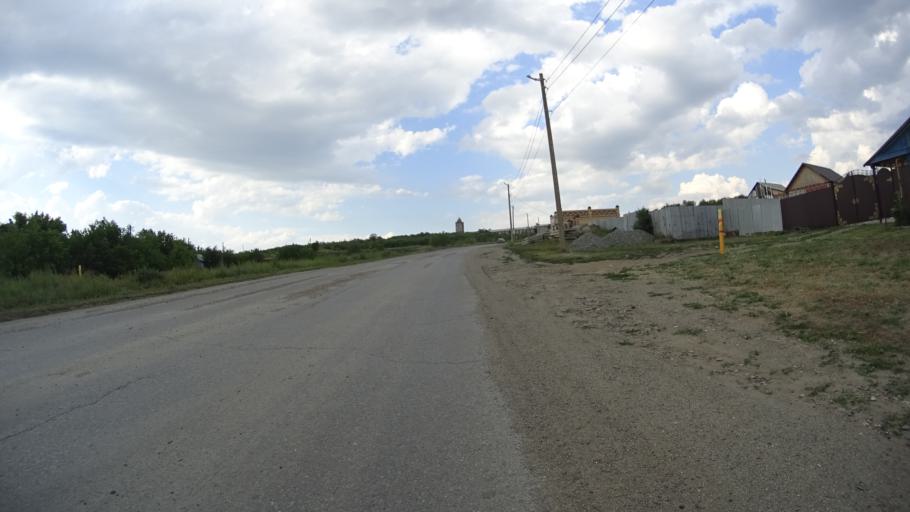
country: RU
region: Chelyabinsk
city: Troitsk
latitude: 54.1001
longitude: 61.5913
